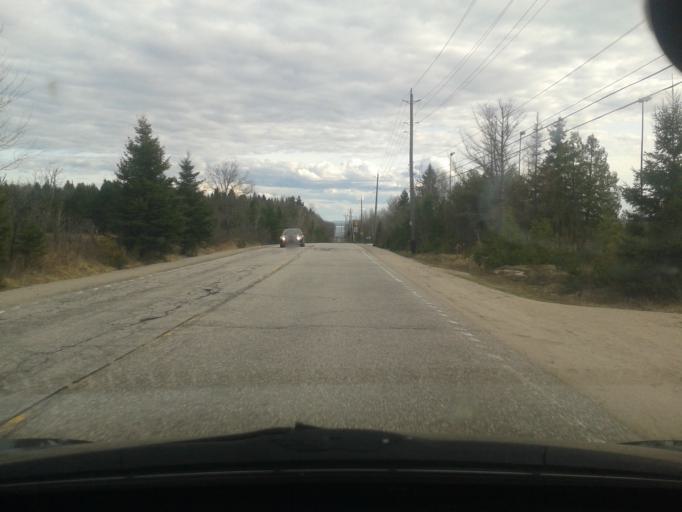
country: CA
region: Ontario
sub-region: Nipissing District
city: North Bay
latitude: 46.3445
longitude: -79.4872
